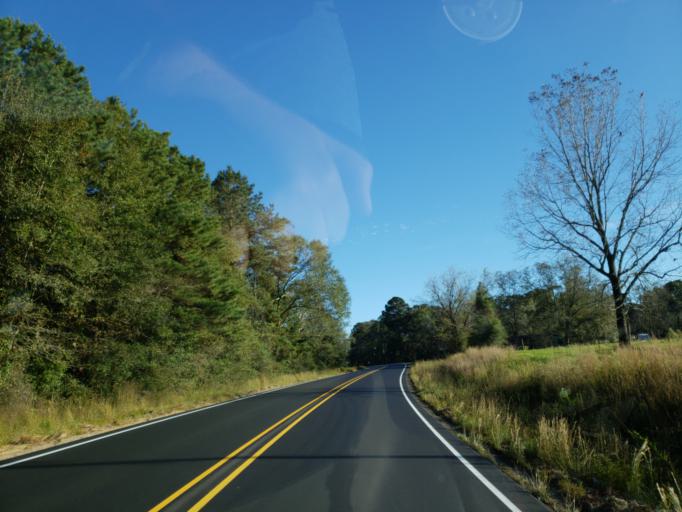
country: US
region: Mississippi
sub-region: Perry County
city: Richton
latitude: 31.3545
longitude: -88.7871
